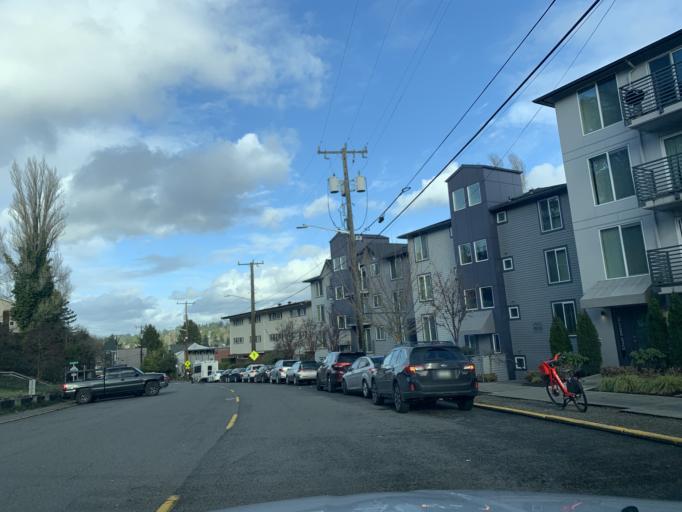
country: US
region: Washington
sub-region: King County
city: Seattle
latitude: 47.6623
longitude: -122.3042
